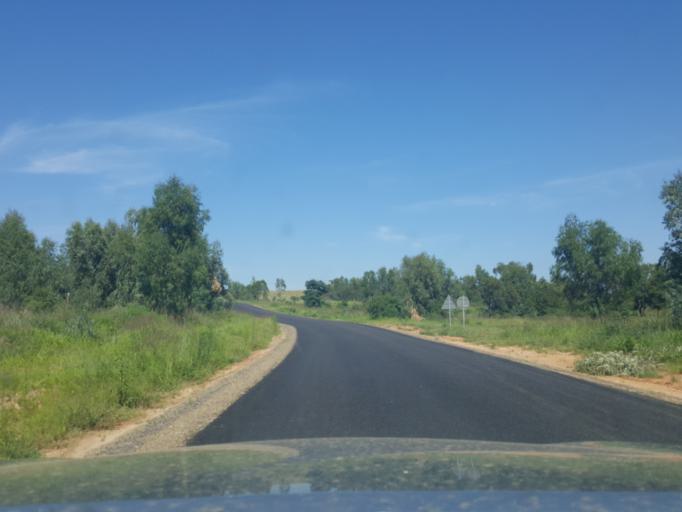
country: ZA
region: Gauteng
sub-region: City of Tshwane Metropolitan Municipality
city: Cullinan
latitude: -25.6845
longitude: 28.5270
